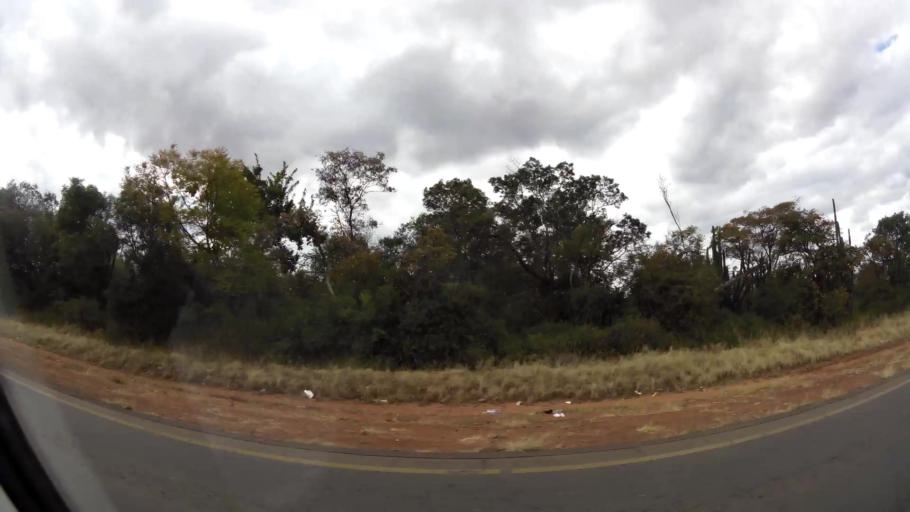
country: ZA
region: Limpopo
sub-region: Waterberg District Municipality
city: Modimolle
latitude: -24.7301
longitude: 28.4302
